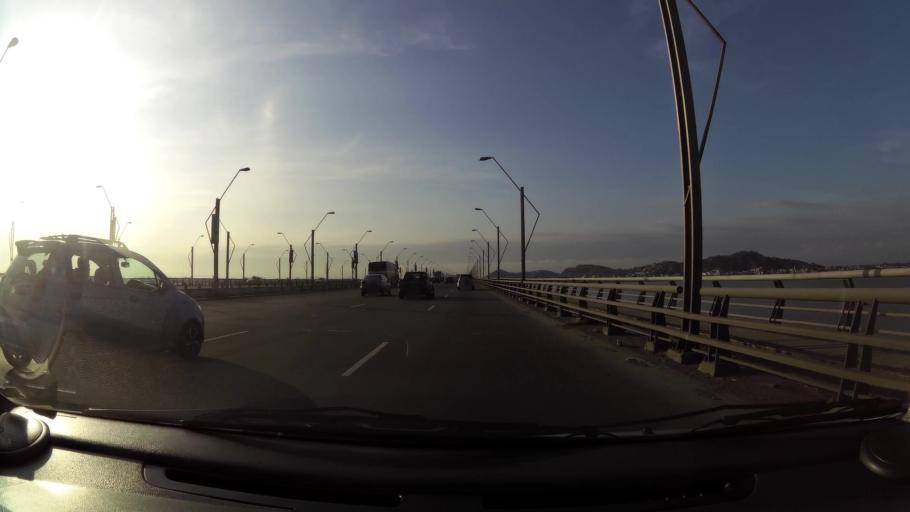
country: EC
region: Guayas
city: Eloy Alfaro
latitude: -2.1578
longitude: -79.8562
